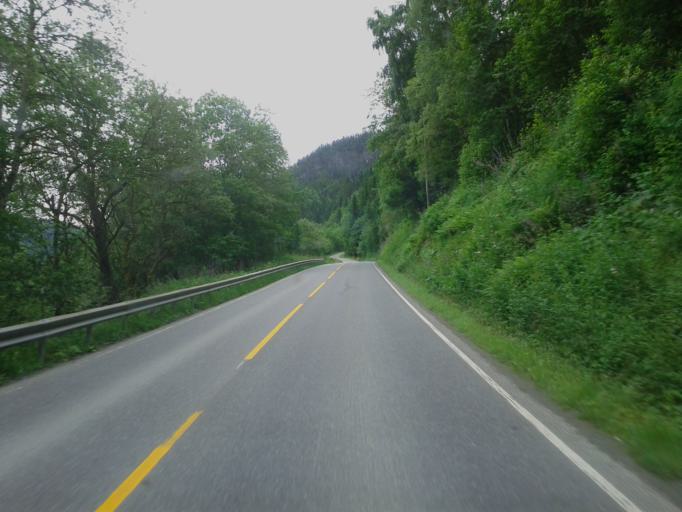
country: NO
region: Sor-Trondelag
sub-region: Midtre Gauldal
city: Storen
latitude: 63.0159
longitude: 10.4319
